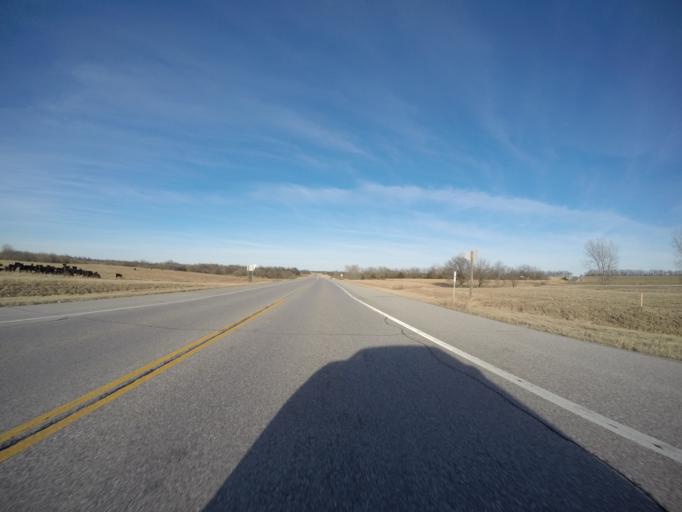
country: US
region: Kansas
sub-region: Marion County
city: Peabody
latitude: 38.1602
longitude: -97.2066
